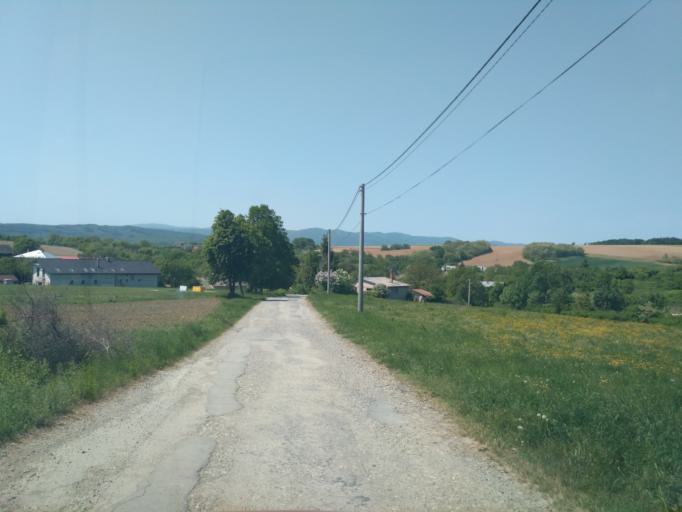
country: SK
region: Kosicky
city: Kosice
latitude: 48.7929
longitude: 21.3596
